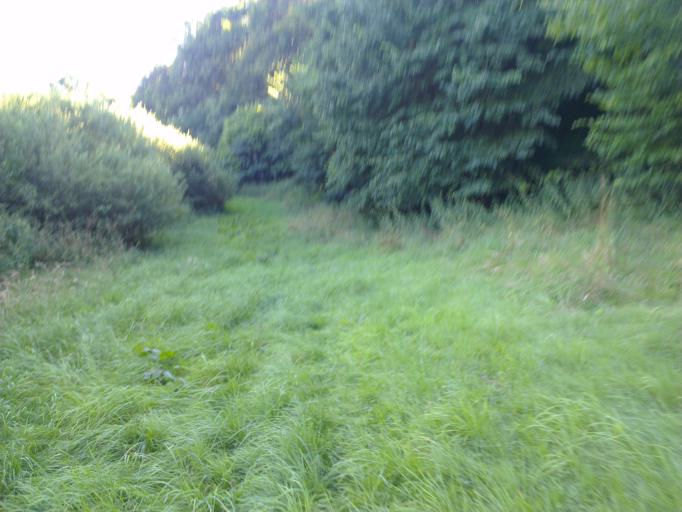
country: DK
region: Capital Region
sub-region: Frederikssund Kommune
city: Skibby
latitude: 55.7703
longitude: 12.0282
